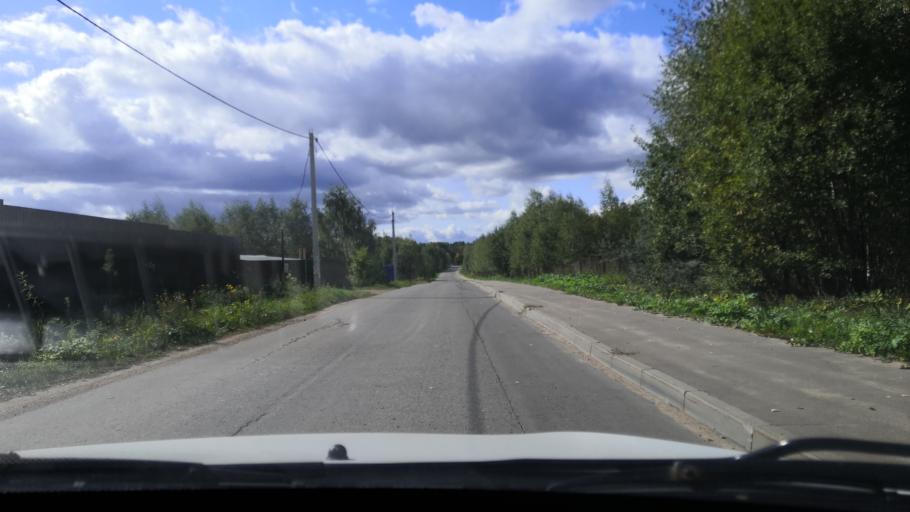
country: RU
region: Moskovskaya
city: Povarovo
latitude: 56.0672
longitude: 37.0477
